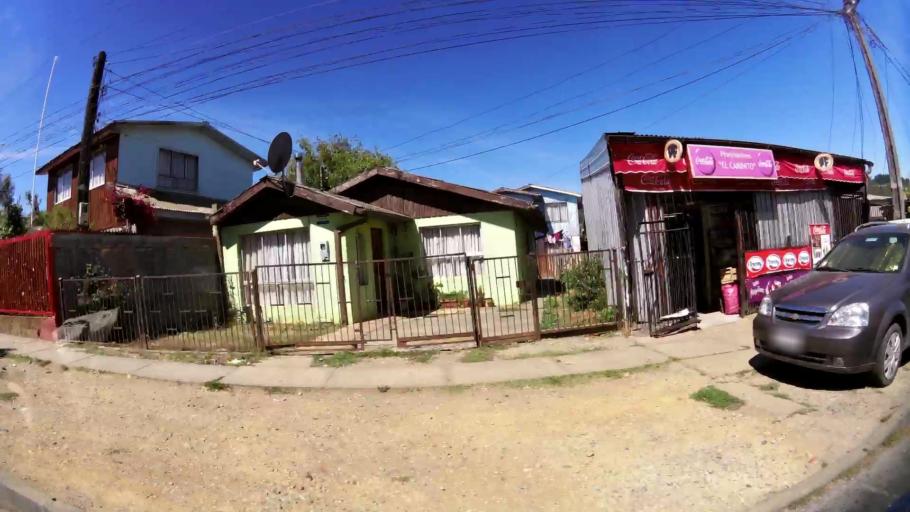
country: CL
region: Biobio
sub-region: Provincia de Concepcion
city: Penco
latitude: -36.7310
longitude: -72.9878
